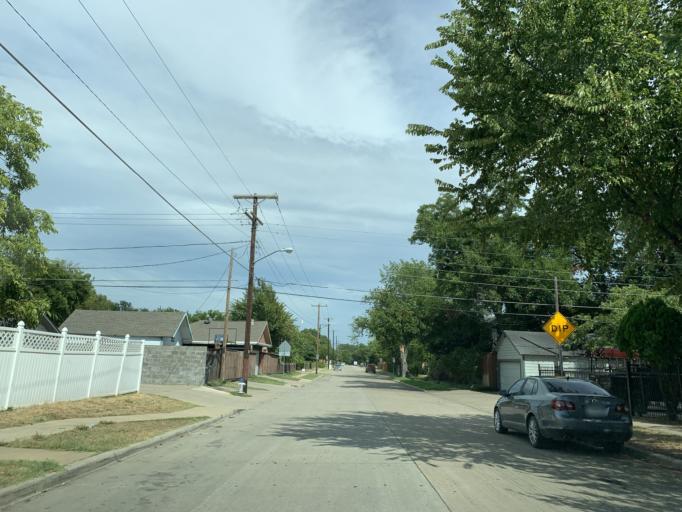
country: US
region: Texas
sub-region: Dallas County
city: Cockrell Hill
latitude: 32.7393
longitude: -96.8439
